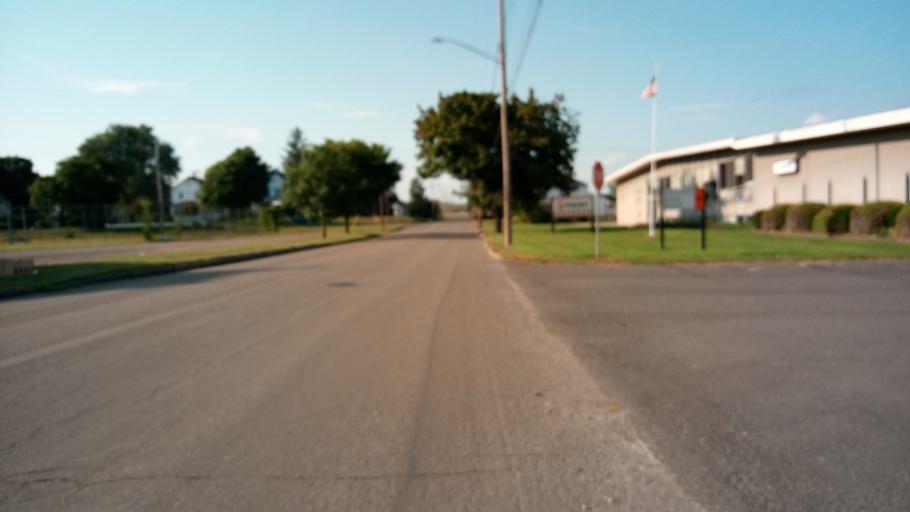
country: US
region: New York
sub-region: Chemung County
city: Elmira Heights
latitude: 42.1132
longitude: -76.8044
